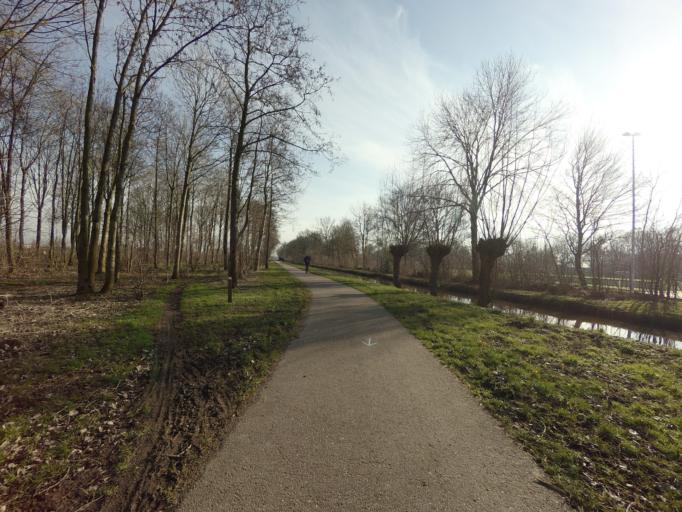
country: NL
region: South Holland
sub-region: Gemeente Giessenlanden
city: Giessenburg
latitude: 51.8489
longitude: 4.8973
